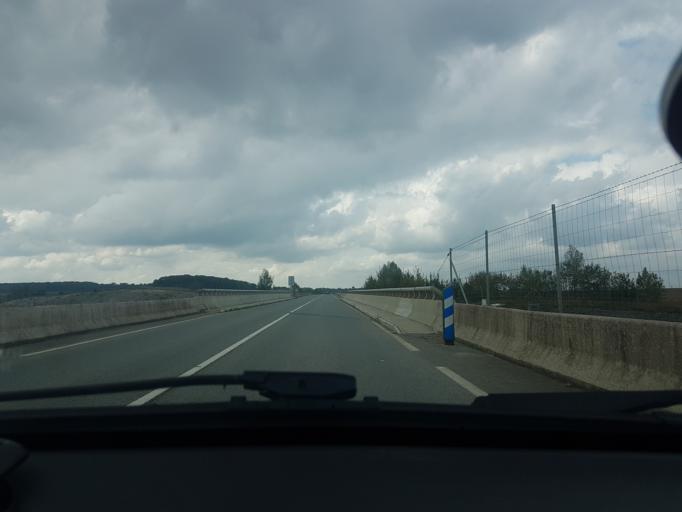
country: FR
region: Franche-Comte
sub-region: Departement de la Haute-Saone
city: Villersexel
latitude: 47.5445
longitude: 6.4809
